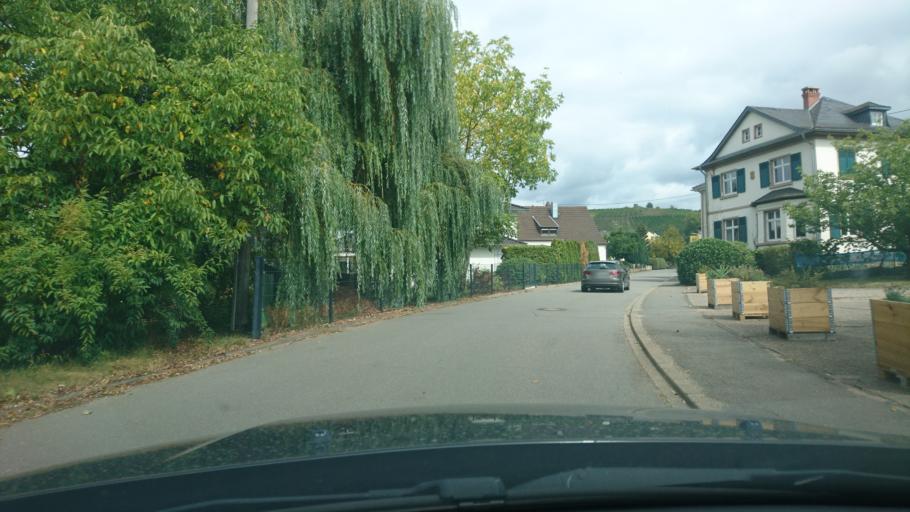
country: DE
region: Rheinland-Pfalz
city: Wiltingen
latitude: 49.6614
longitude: 6.5906
